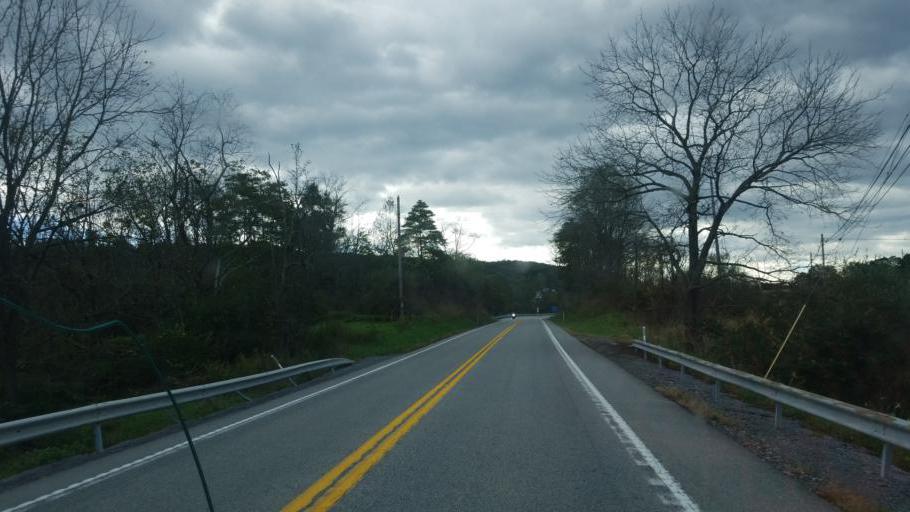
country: US
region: Pennsylvania
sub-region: Fulton County
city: McConnellsburg
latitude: 39.9498
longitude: -78.0222
